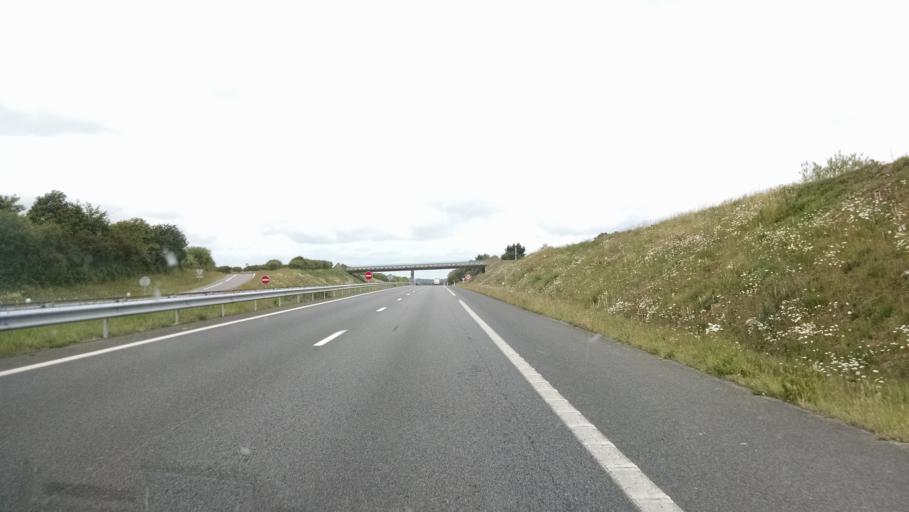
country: FR
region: Brittany
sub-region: Departement du Morbihan
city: Nivillac
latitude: 47.5192
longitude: -2.2796
